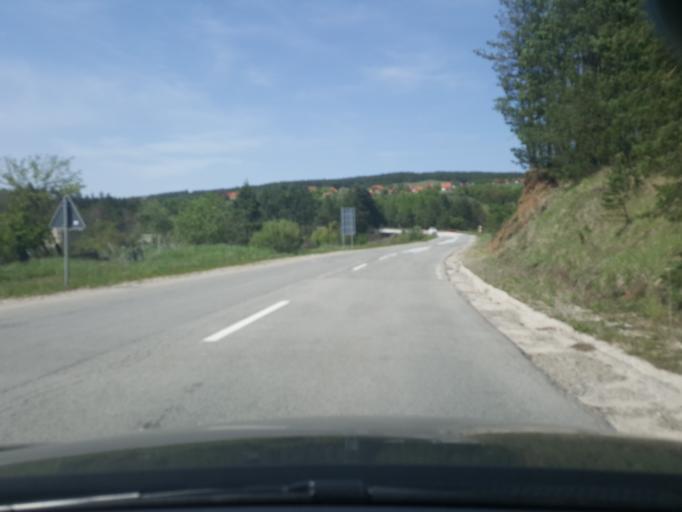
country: RS
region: Central Serbia
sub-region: Zlatiborski Okrug
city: Bajina Basta
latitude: 43.8389
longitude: 19.6054
